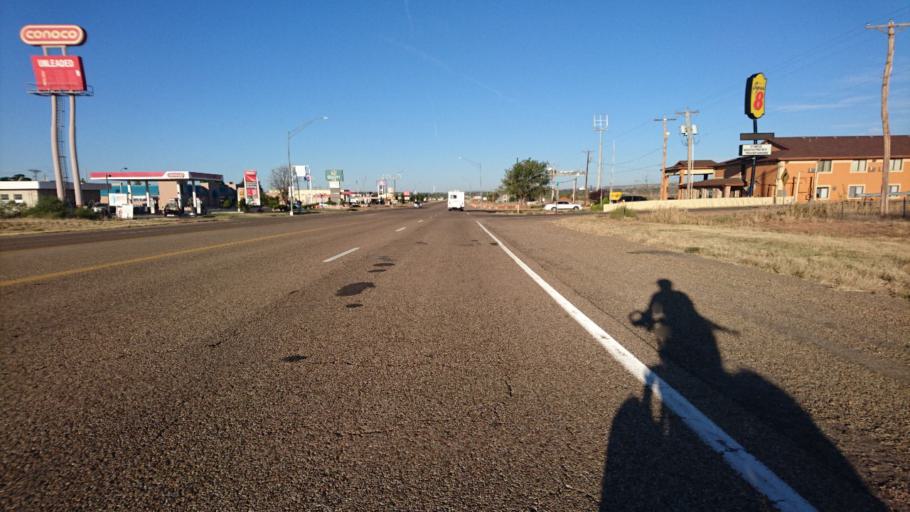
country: US
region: New Mexico
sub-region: Quay County
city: Tucumcari
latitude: 35.1720
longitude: -103.6793
